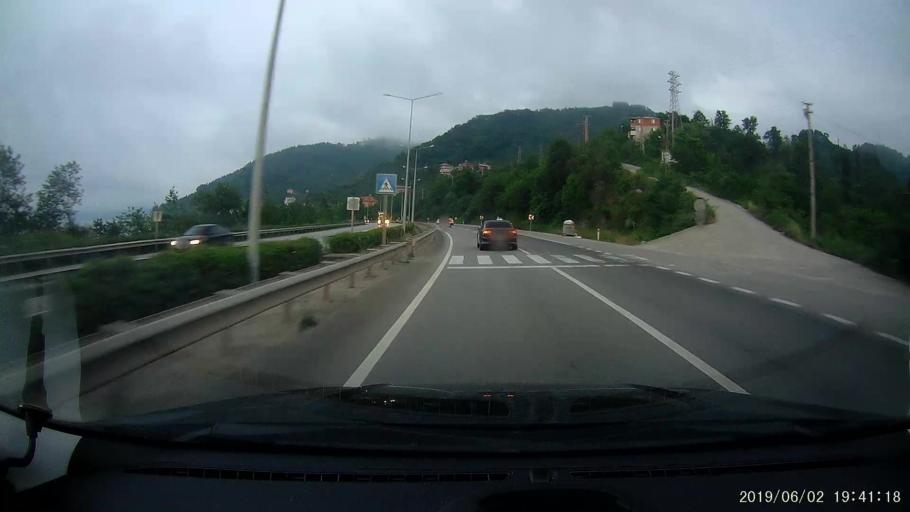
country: TR
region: Giresun
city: Kesap
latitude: 40.9145
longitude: 38.4772
